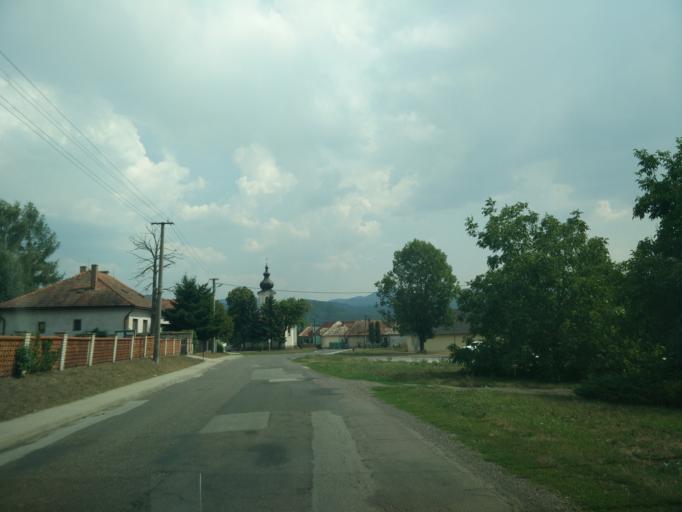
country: SK
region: Banskobystricky
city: Zarnovica
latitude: 48.5456
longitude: 18.7622
